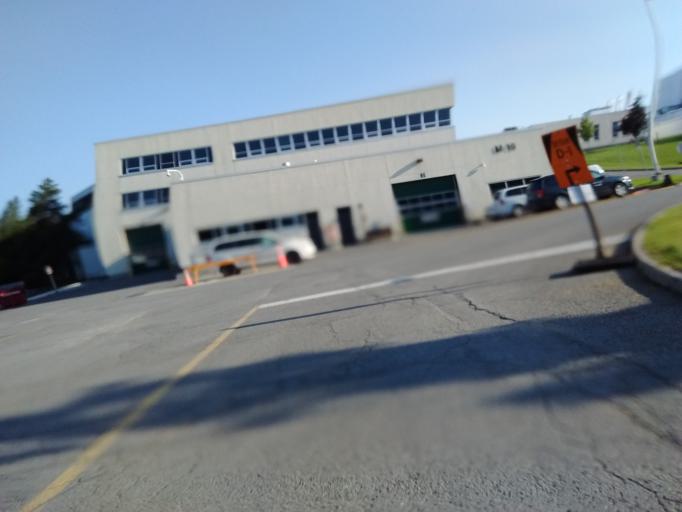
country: CA
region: Quebec
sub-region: Outaouais
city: Gatineau
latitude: 45.4521
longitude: -75.6191
